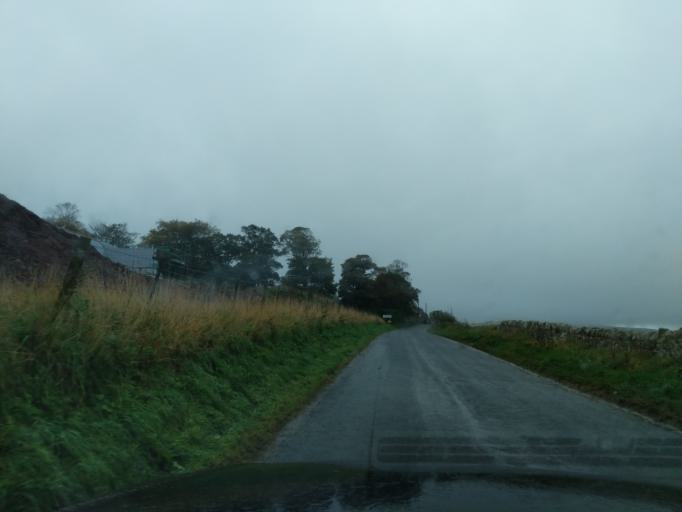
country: GB
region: Scotland
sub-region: East Lothian
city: Dunbar
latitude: 55.9567
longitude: -2.4392
